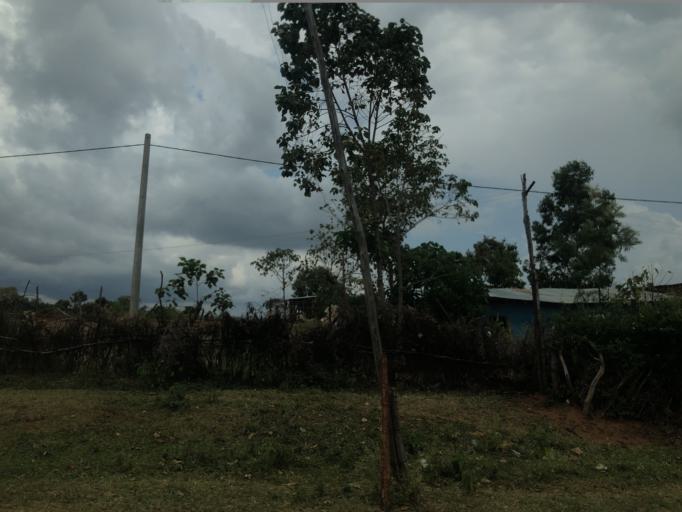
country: ET
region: Southern Nations, Nationalities, and People's Region
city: Jinka
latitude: 5.5258
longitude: 36.7296
